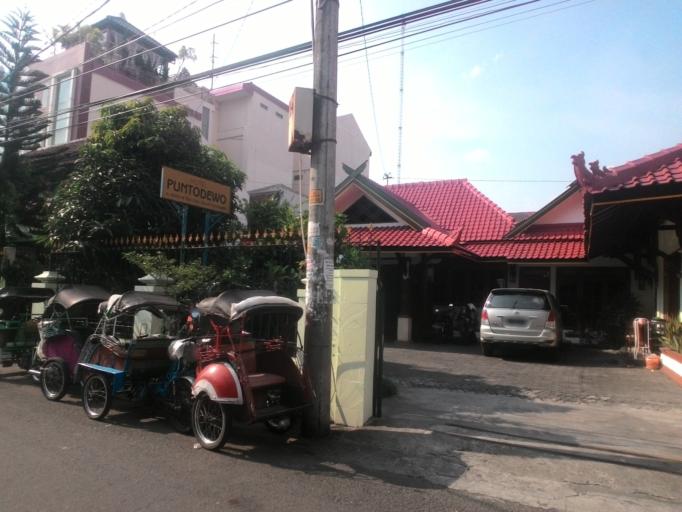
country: ID
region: Daerah Istimewa Yogyakarta
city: Yogyakarta
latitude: -7.7938
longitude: 110.3633
